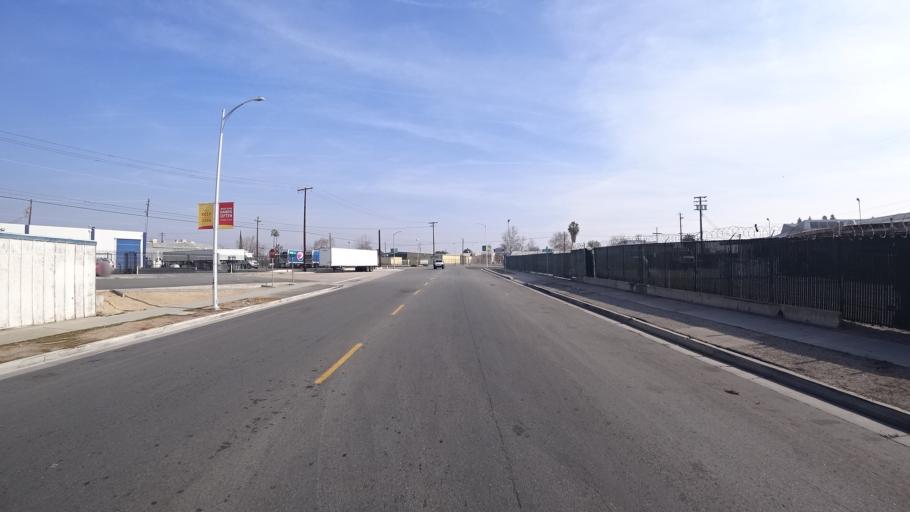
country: US
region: California
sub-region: Kern County
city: Bakersfield
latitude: 35.3762
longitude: -119.0009
